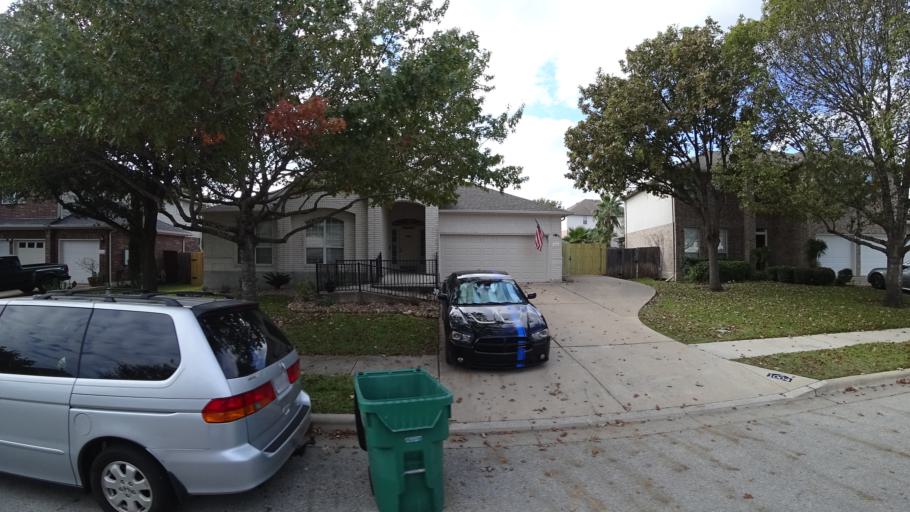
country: US
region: Texas
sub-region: Travis County
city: Pflugerville
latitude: 30.4293
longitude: -97.6261
